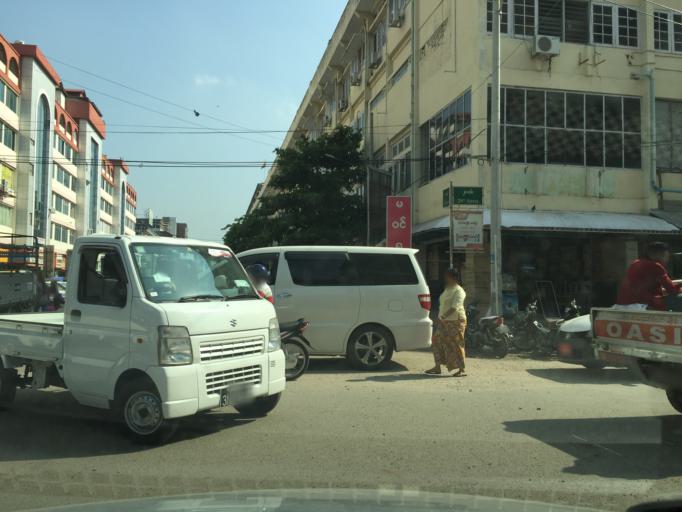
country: MM
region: Mandalay
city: Mandalay
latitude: 21.9805
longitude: 96.0777
